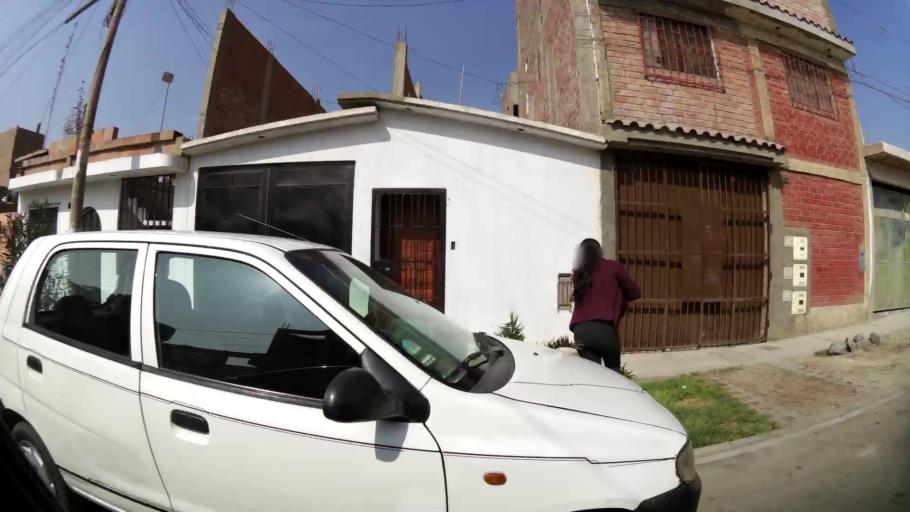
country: PE
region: Lima
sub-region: Lima
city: Santa Rosa
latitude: -11.7775
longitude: -77.1654
